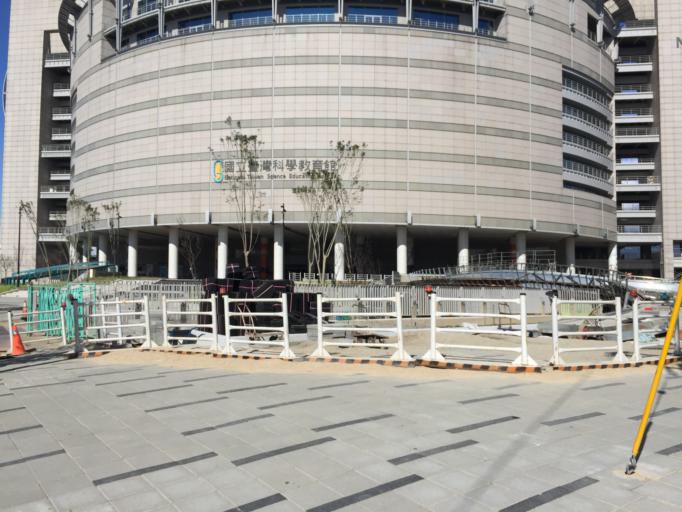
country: TW
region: Taipei
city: Taipei
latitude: 25.0950
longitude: 121.5168
